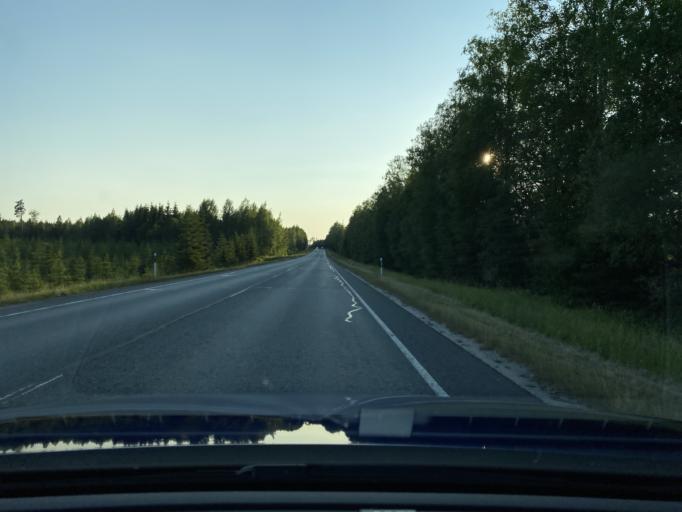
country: FI
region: Haeme
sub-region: Forssa
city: Tammela
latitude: 60.8280
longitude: 23.8920
